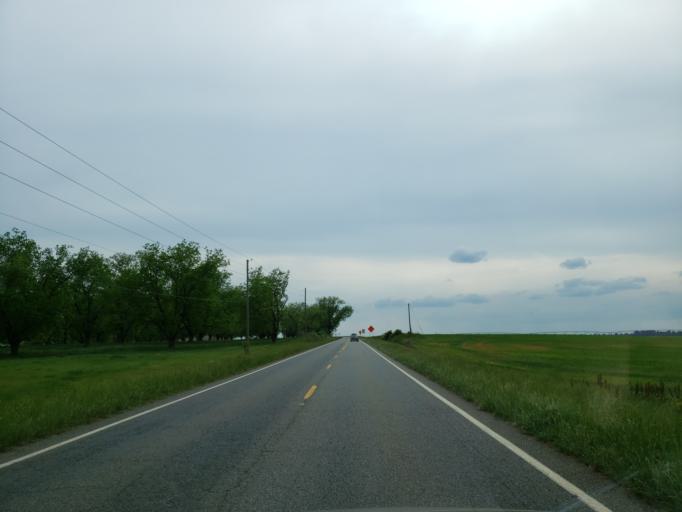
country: US
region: Georgia
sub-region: Macon County
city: Marshallville
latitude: 32.3646
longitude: -83.9199
